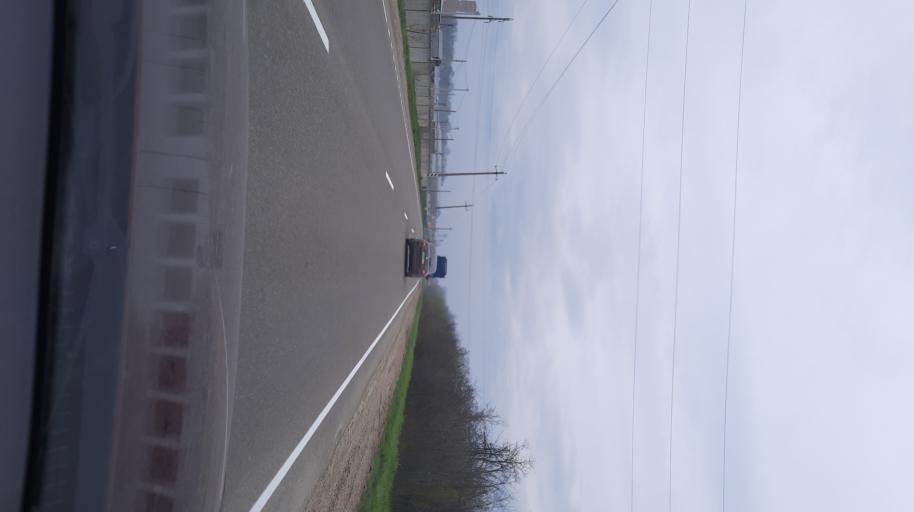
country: RU
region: Krasnodarskiy
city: Timashevsk
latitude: 45.6390
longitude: 38.9145
